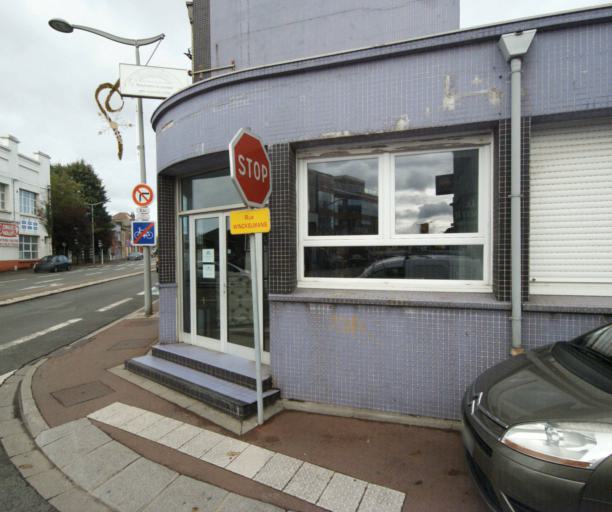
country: FR
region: Nord-Pas-de-Calais
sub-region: Departement du Nord
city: Lomme
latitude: 50.6466
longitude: 3.0089
